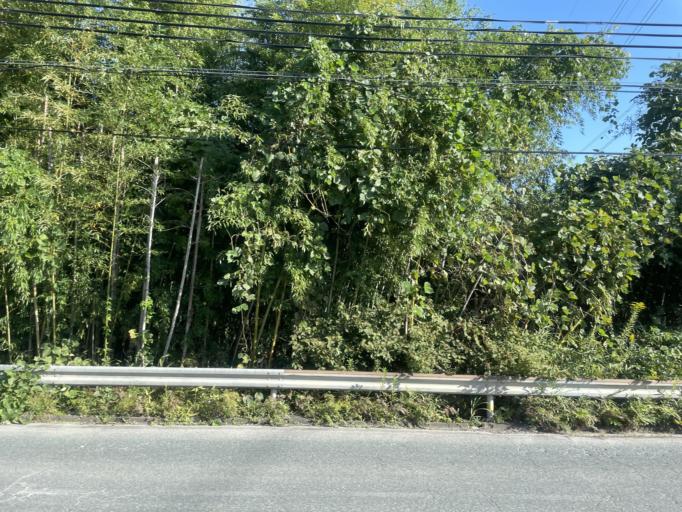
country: JP
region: Osaka
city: Kashihara
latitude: 34.5419
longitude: 135.6769
